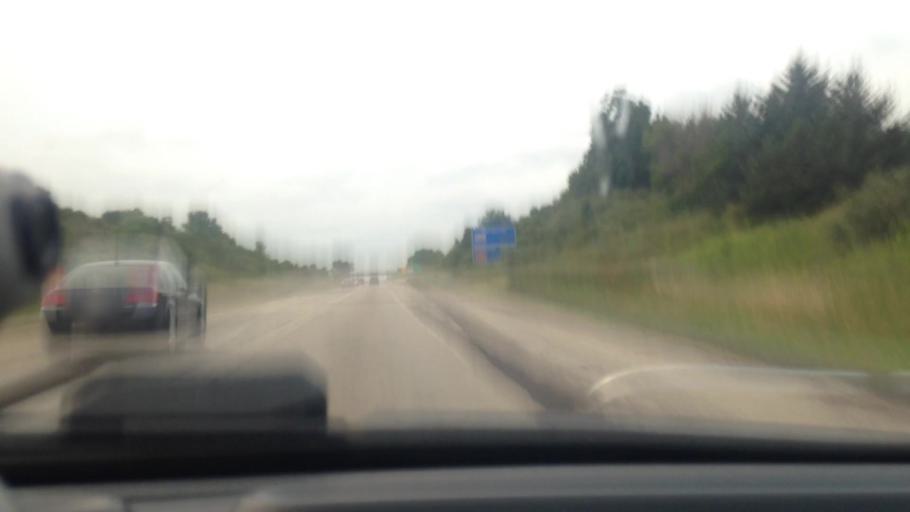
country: US
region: Wisconsin
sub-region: Washington County
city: Richfield
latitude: 43.2756
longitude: -88.1848
